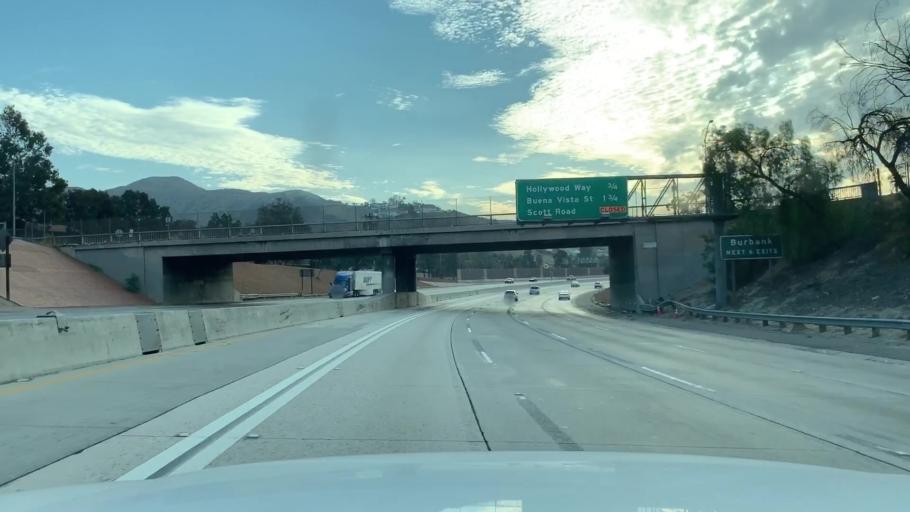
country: US
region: California
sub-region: Los Angeles County
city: North Hollywood
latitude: 34.2216
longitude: -118.3604
